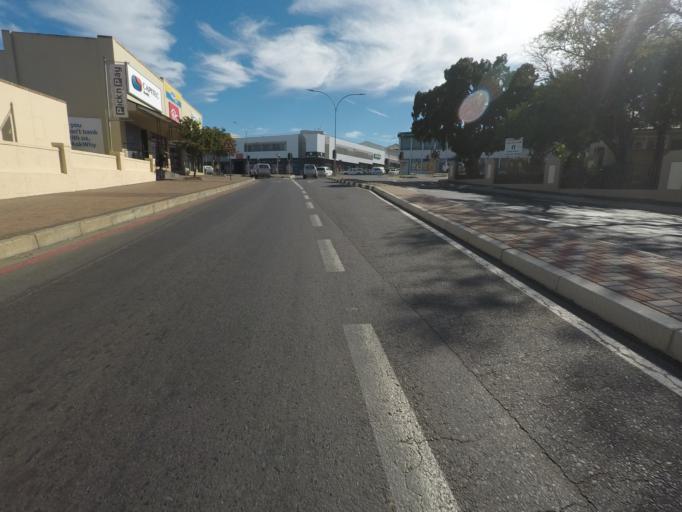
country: ZA
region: Western Cape
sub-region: West Coast District Municipality
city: Malmesbury
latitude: -33.4629
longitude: 18.7295
